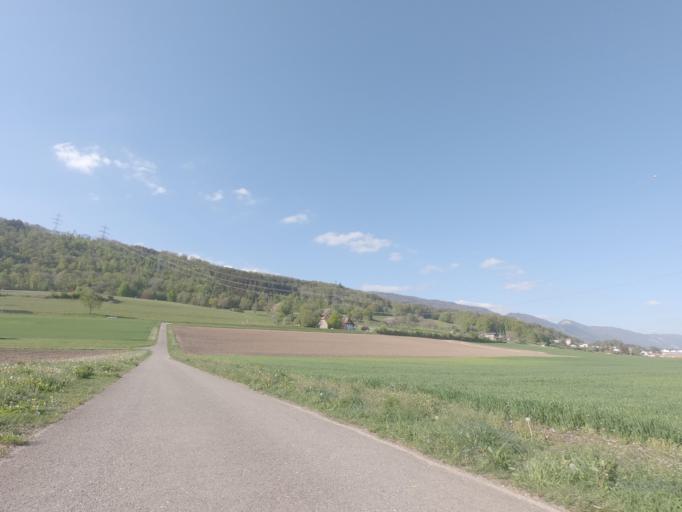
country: CH
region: Bern
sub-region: Biel/Bienne District
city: Pieterlen
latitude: 47.1747
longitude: 7.3500
